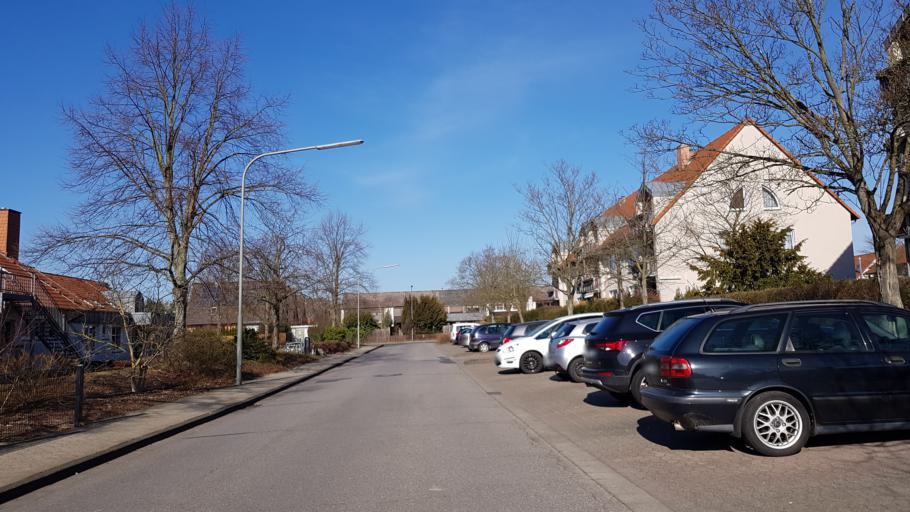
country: DE
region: Lower Saxony
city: Gifhorn
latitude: 52.4860
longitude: 10.5651
